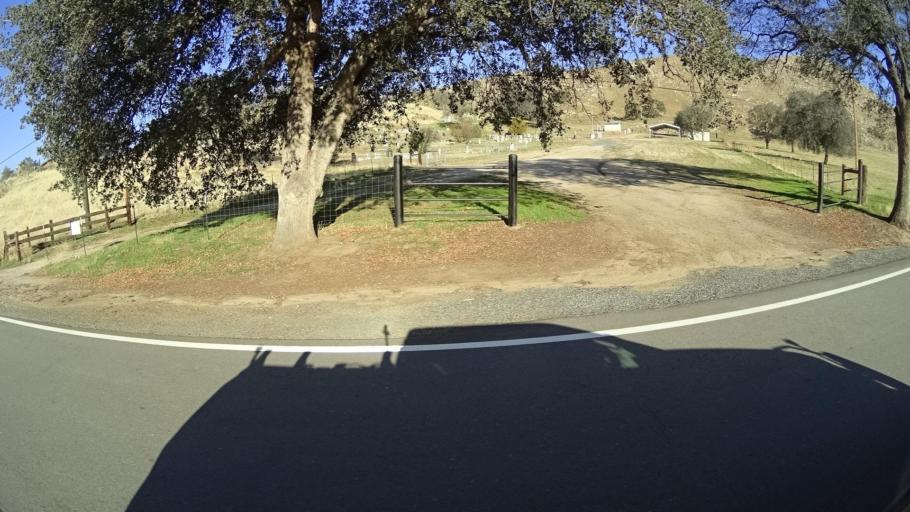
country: US
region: California
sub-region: Kern County
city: Alta Sierra
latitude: 35.7055
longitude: -118.8318
